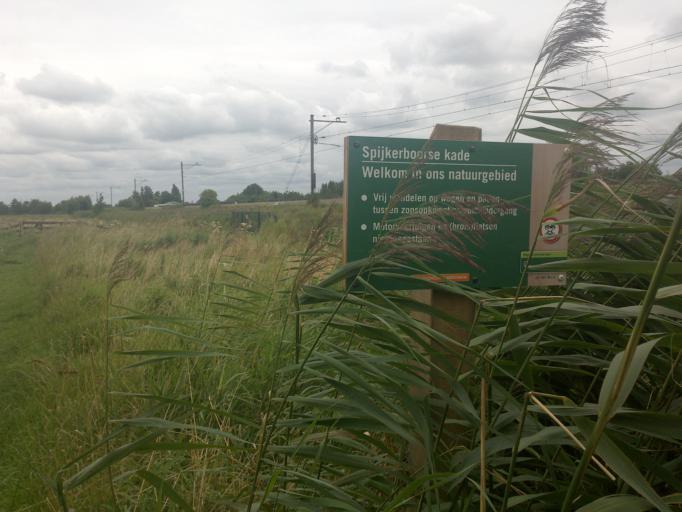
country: NL
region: South Holland
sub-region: Gemeente Boskoop
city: Boskoop
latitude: 52.0964
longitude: 4.6505
